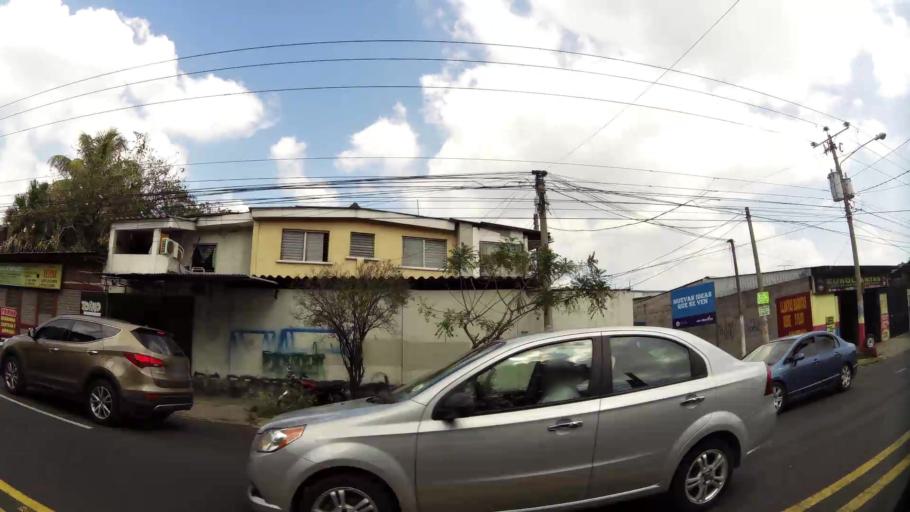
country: SV
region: San Salvador
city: Mejicanos
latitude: 13.7095
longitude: -89.2302
